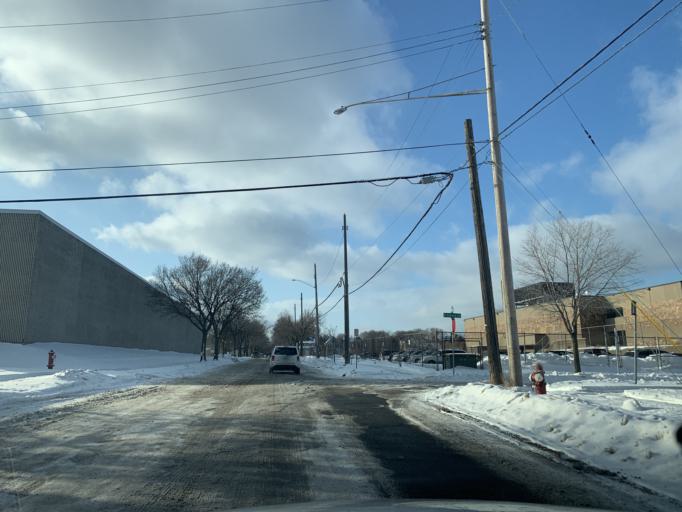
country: US
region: Minnesota
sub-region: Hennepin County
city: Minneapolis
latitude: 44.9931
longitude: -93.2893
